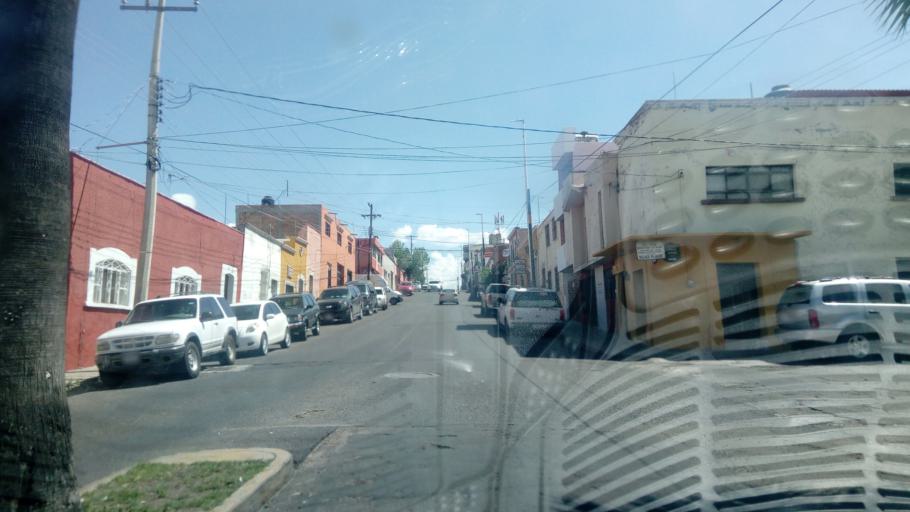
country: MX
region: Durango
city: Victoria de Durango
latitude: 24.0182
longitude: -104.6732
